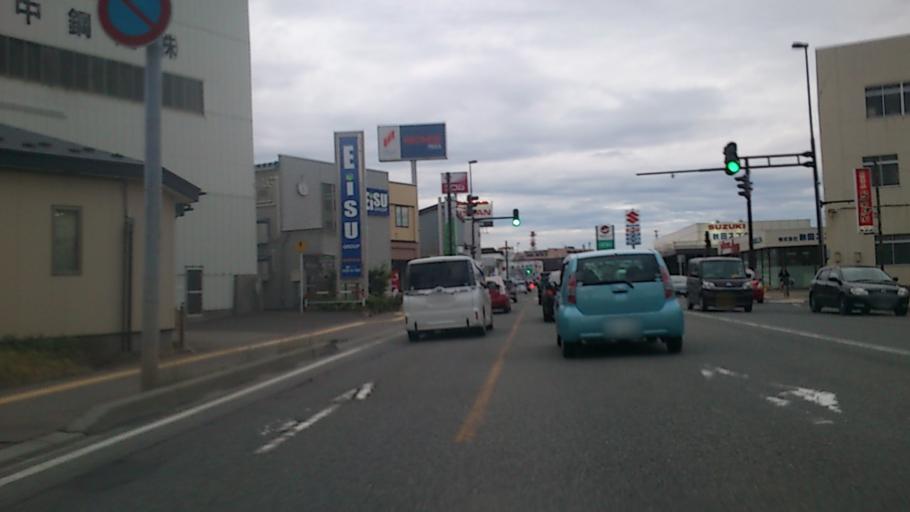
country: JP
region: Akita
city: Akita Shi
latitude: 39.7275
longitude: 140.1058
